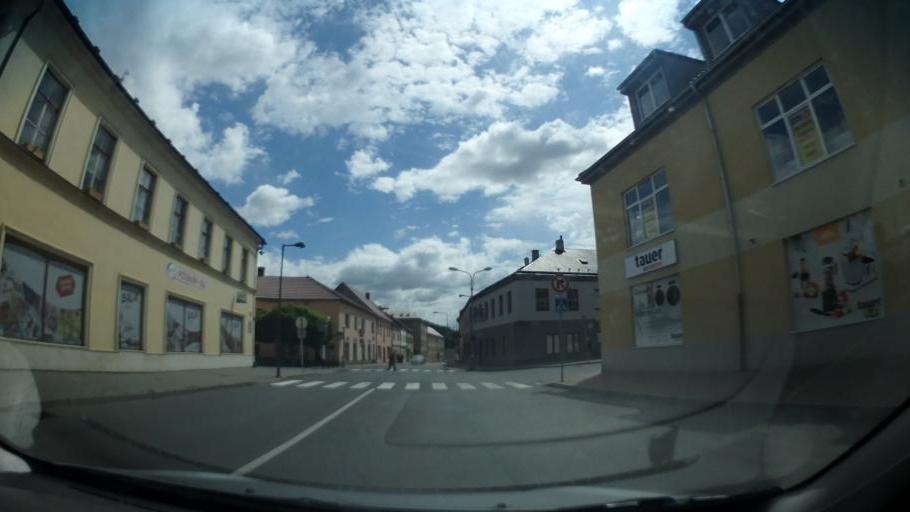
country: CZ
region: Pardubicky
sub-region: Okres Svitavy
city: Moravska Trebova
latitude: 49.7581
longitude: 16.6608
